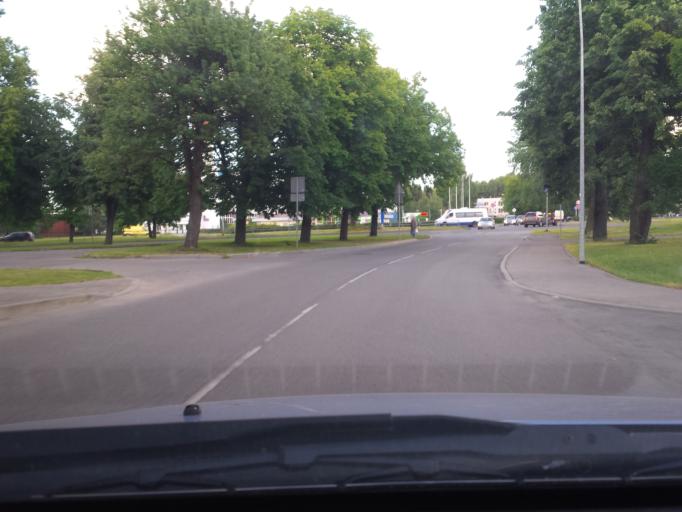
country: LV
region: Marupe
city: Marupe
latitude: 56.9610
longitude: 24.0334
